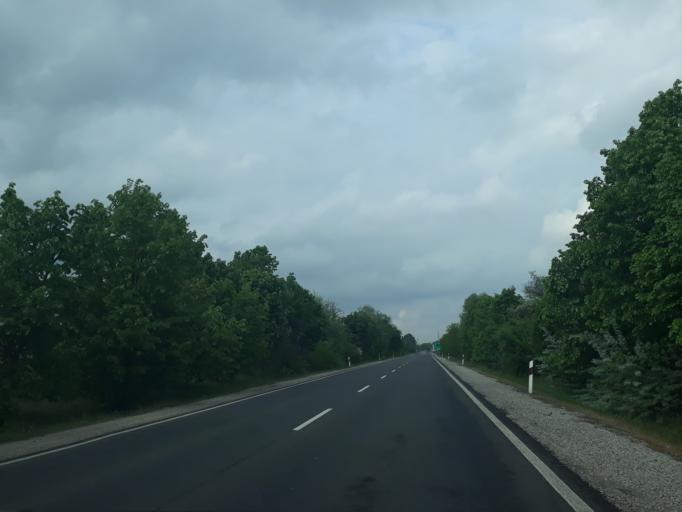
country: HU
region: Szabolcs-Szatmar-Bereg
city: Ajak
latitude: 48.2011
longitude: 22.0479
